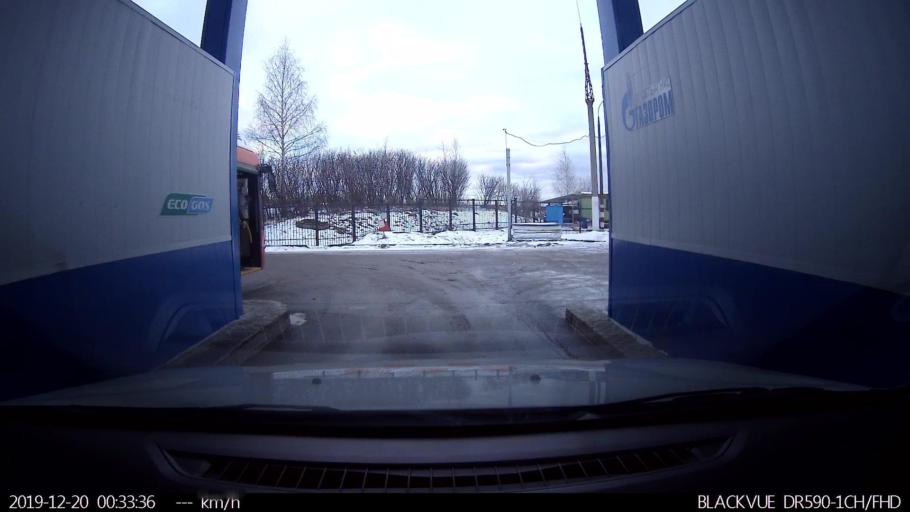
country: RU
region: Vladimir
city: Yur'yev-Pol'skiy
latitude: 56.4626
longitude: 39.6970
